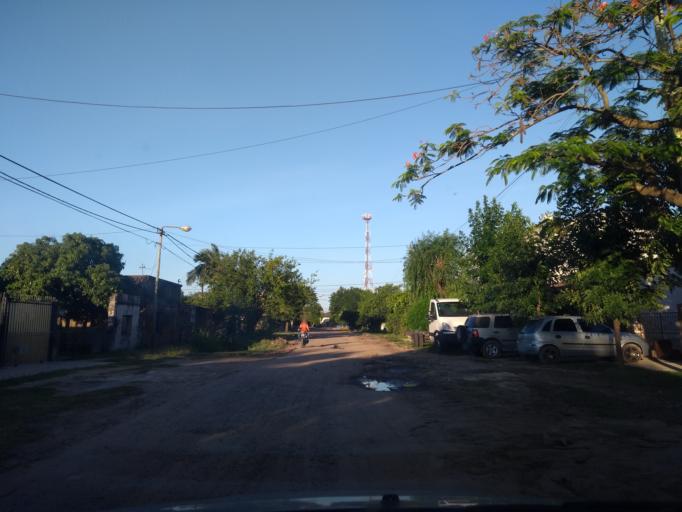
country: AR
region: Chaco
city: Barranqueras
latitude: -27.4851
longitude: -58.9439
